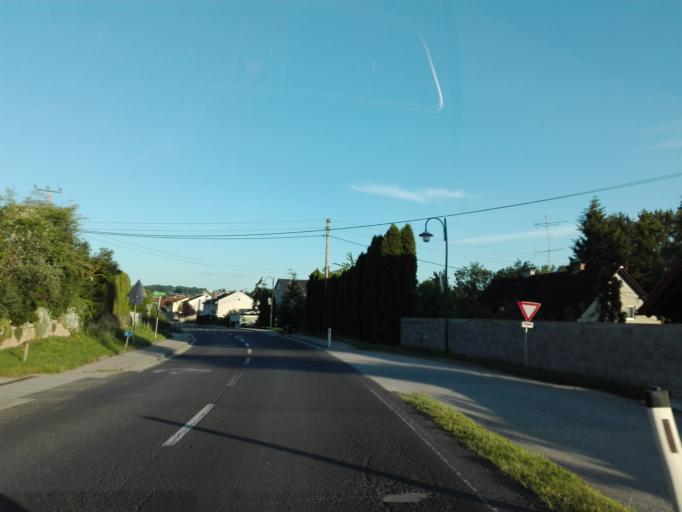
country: AT
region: Upper Austria
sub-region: Politischer Bezirk Urfahr-Umgebung
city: Ottensheim
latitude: 48.2832
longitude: 14.1472
